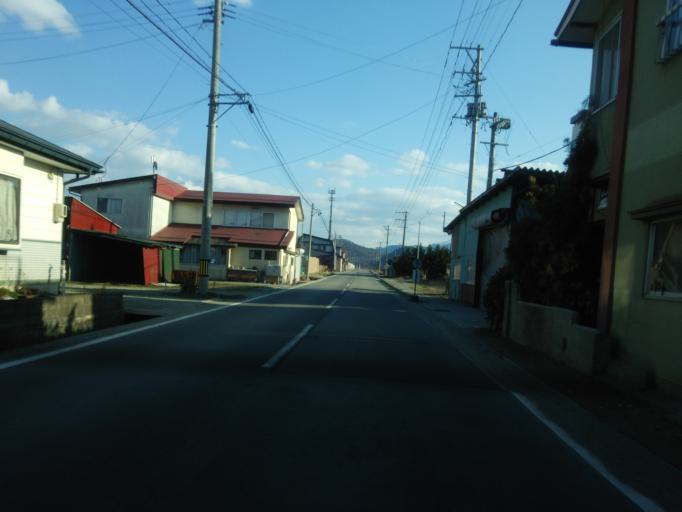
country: JP
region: Fukushima
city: Kitakata
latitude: 37.4734
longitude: 139.8959
